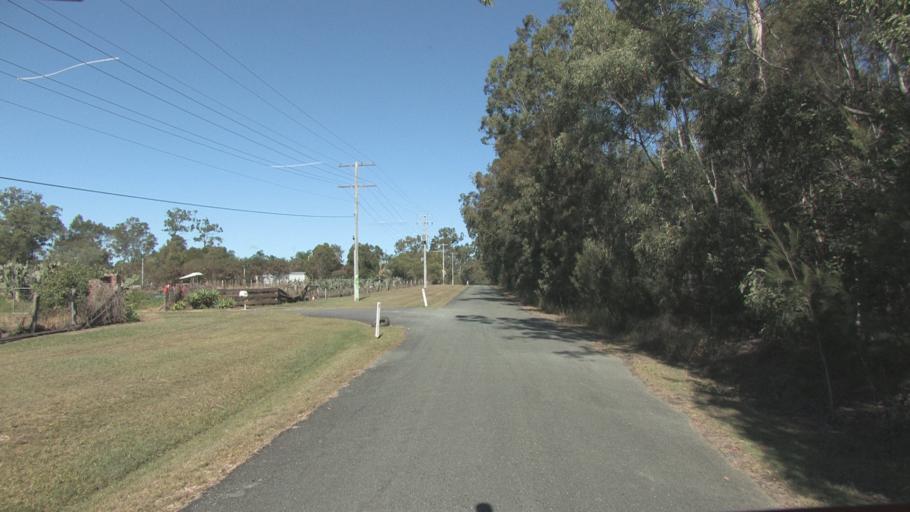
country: AU
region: Queensland
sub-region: Logan
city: Park Ridge South
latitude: -27.7000
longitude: 153.0037
